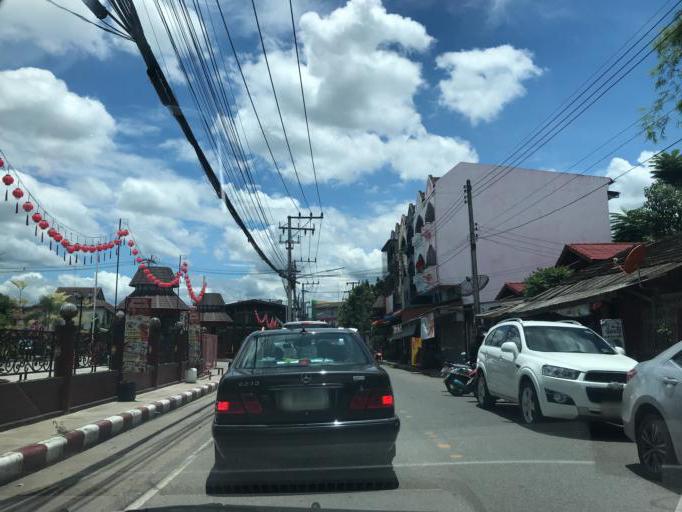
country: TH
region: Chiang Mai
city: Chiang Mai
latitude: 18.7755
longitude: 98.9826
